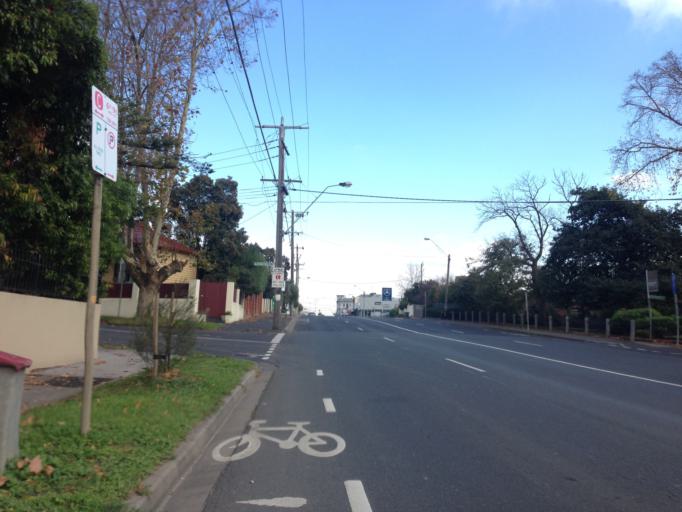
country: AU
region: Victoria
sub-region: Darebin
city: Fairfield
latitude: -37.7827
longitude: 145.0213
